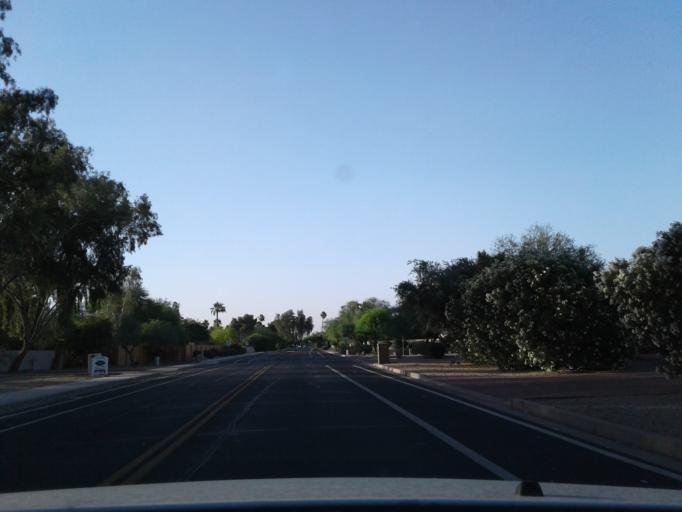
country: US
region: Arizona
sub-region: Maricopa County
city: Paradise Valley
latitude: 33.5711
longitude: -111.9691
